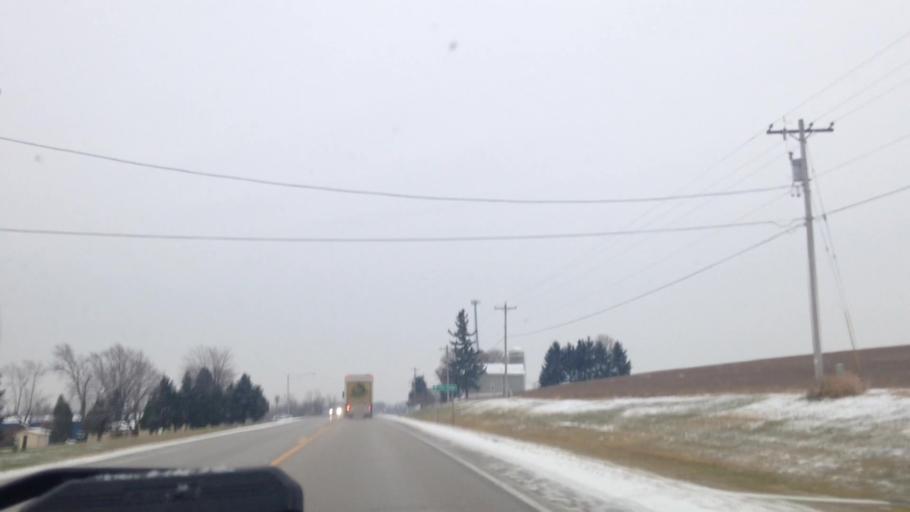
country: US
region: Wisconsin
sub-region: Dodge County
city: Hustisford
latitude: 43.4016
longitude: -88.5420
